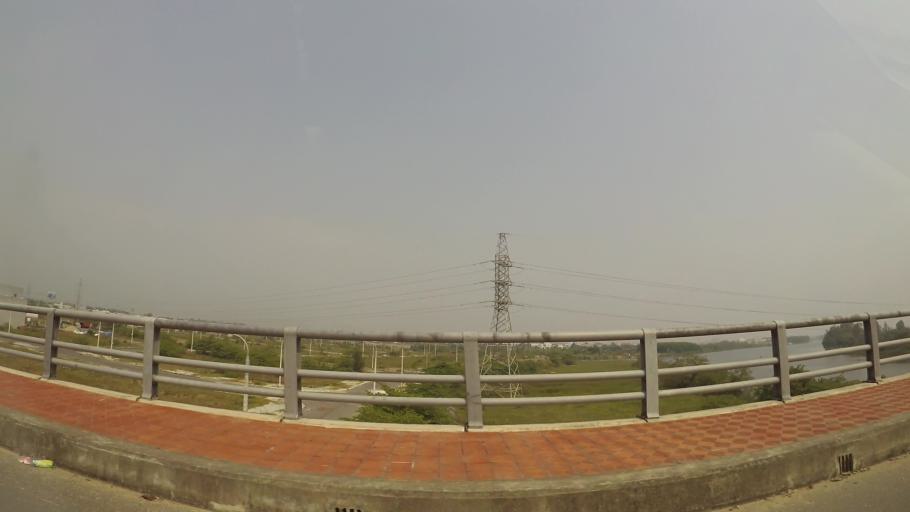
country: VN
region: Da Nang
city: Cam Le
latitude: 15.9687
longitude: 108.2161
